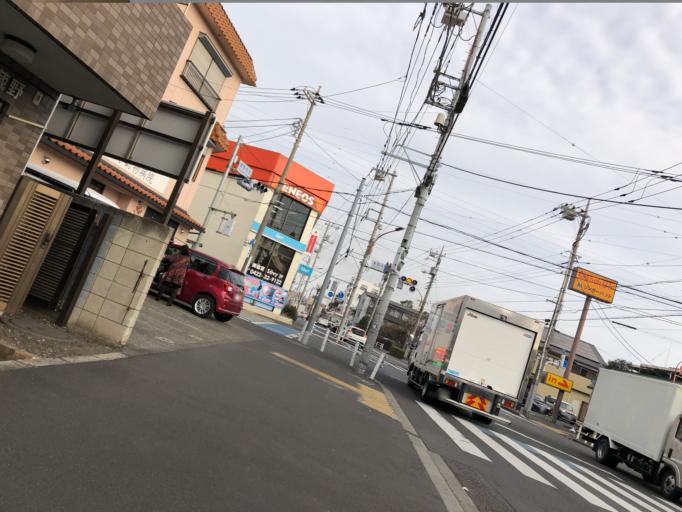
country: JP
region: Tokyo
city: Kamirenjaku
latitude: 35.6899
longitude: 139.5458
